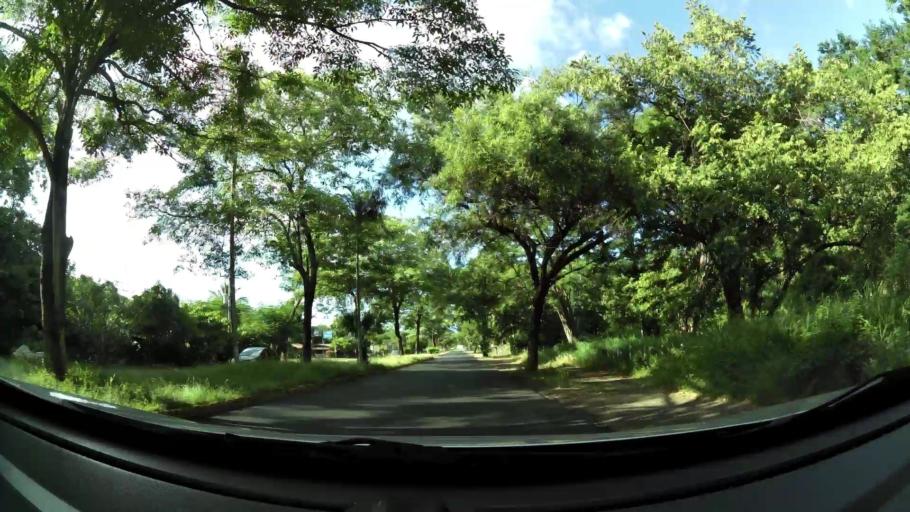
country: CR
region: Guanacaste
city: Sardinal
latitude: 10.5427
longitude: -85.6921
